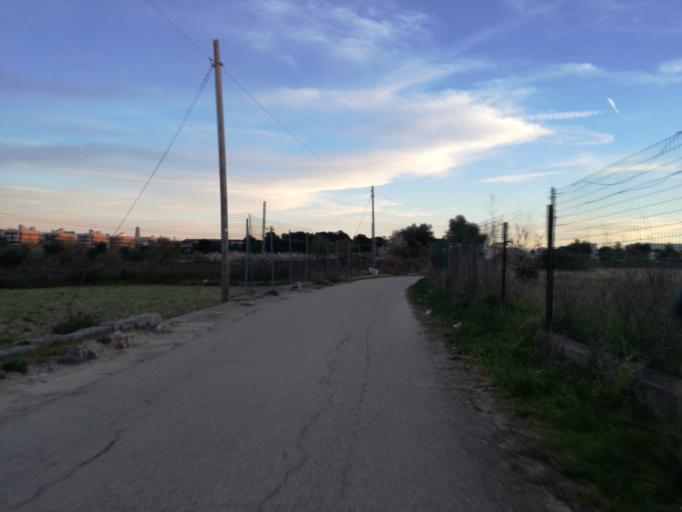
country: IT
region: Apulia
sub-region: Provincia di Bari
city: Adelfia
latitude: 41.0103
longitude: 16.8719
